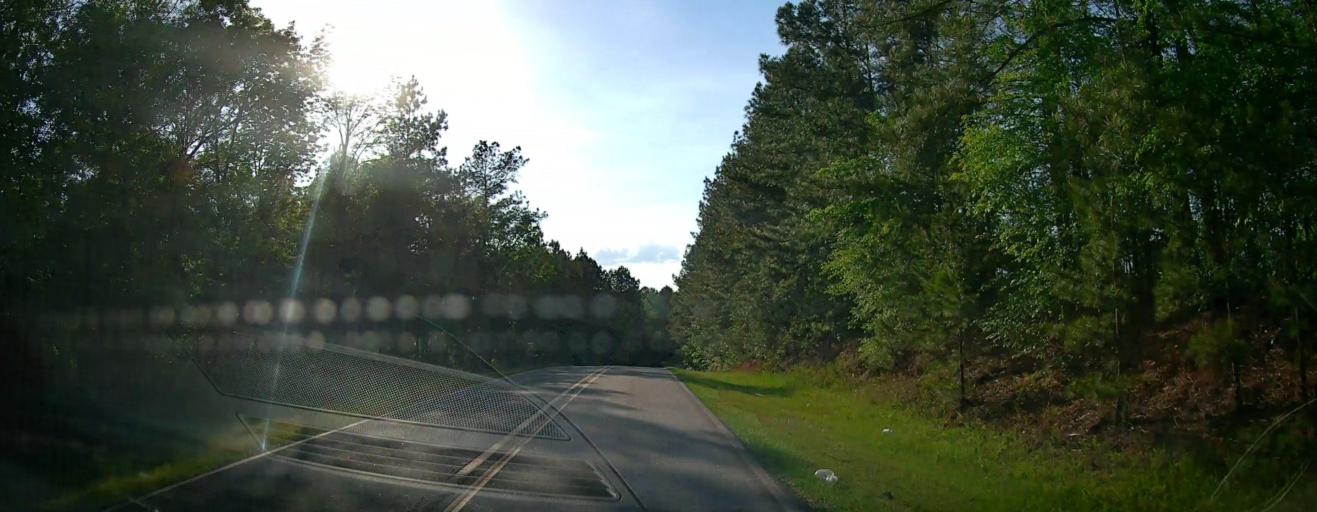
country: US
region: Georgia
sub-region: Putnam County
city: Eatonton
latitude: 33.2733
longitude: -83.3059
